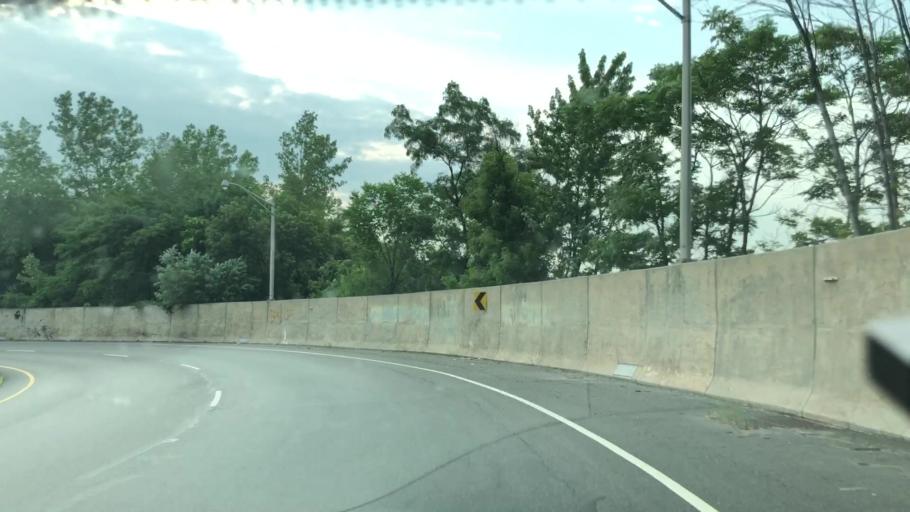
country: US
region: New Jersey
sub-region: Bergen County
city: Elmwood Park
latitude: 40.8953
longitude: -74.1317
